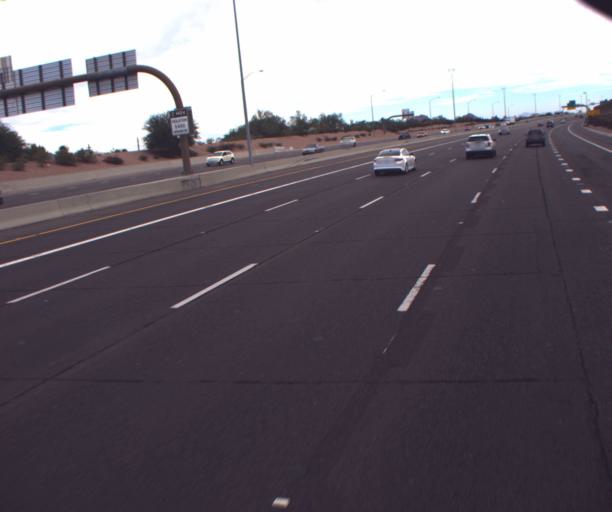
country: US
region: Arizona
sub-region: Maricopa County
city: Phoenix
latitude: 33.4619
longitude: -112.0207
